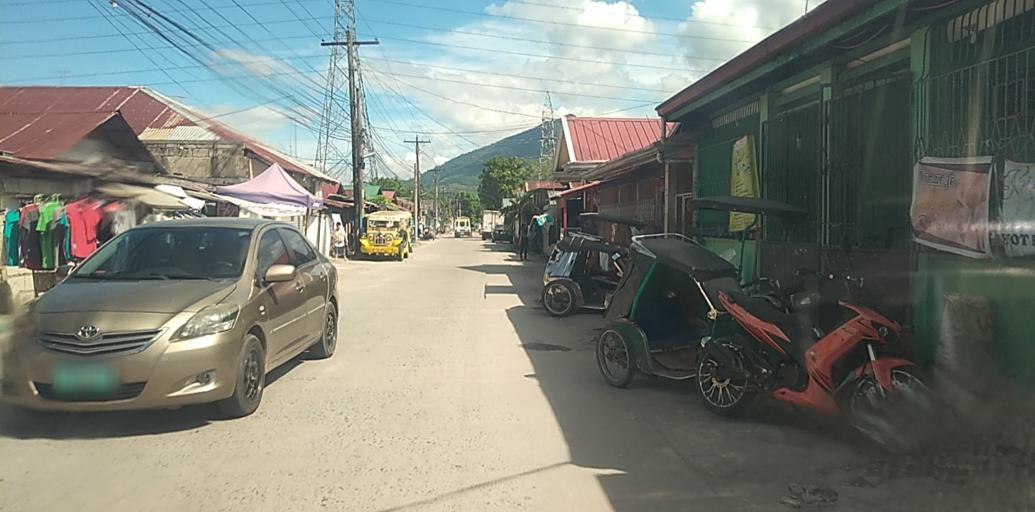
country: PH
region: Central Luzon
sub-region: Province of Pampanga
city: Buensuseso
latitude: 15.1936
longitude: 120.6707
